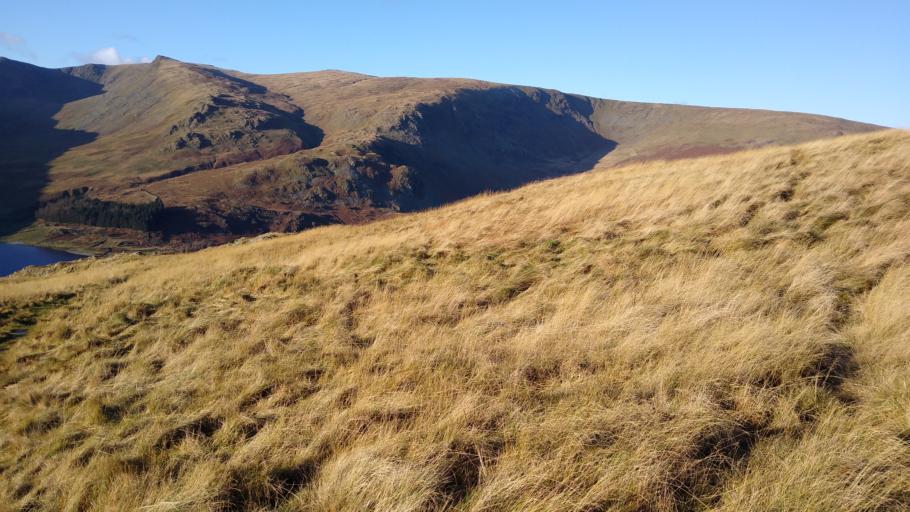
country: GB
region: England
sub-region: Cumbria
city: Windermere
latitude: 54.4998
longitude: -2.7968
